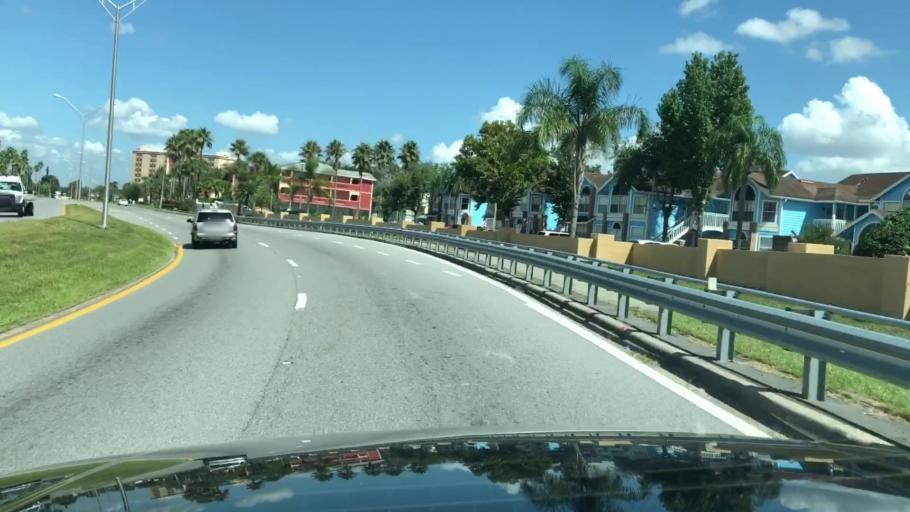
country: US
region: Florida
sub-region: Osceola County
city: Celebration
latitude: 28.3271
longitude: -81.4895
